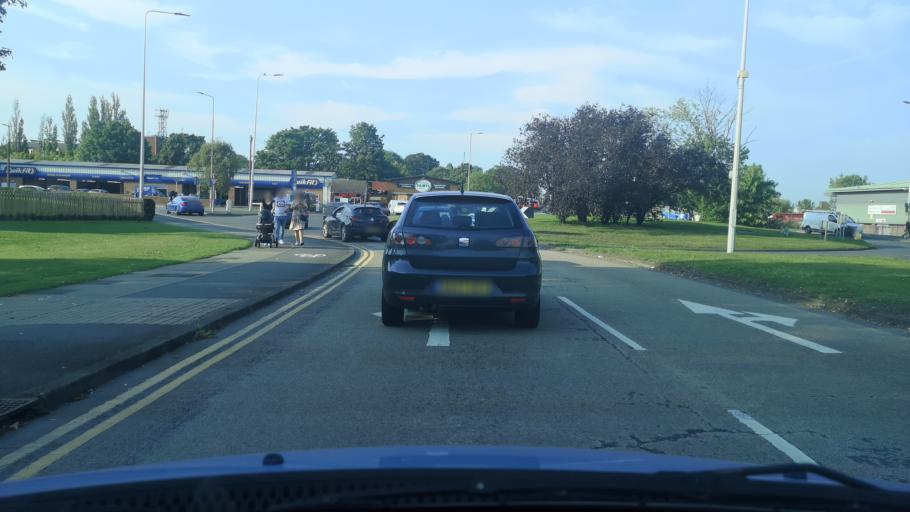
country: GB
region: England
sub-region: North Lincolnshire
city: Scunthorpe
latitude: 53.5841
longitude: -0.6536
